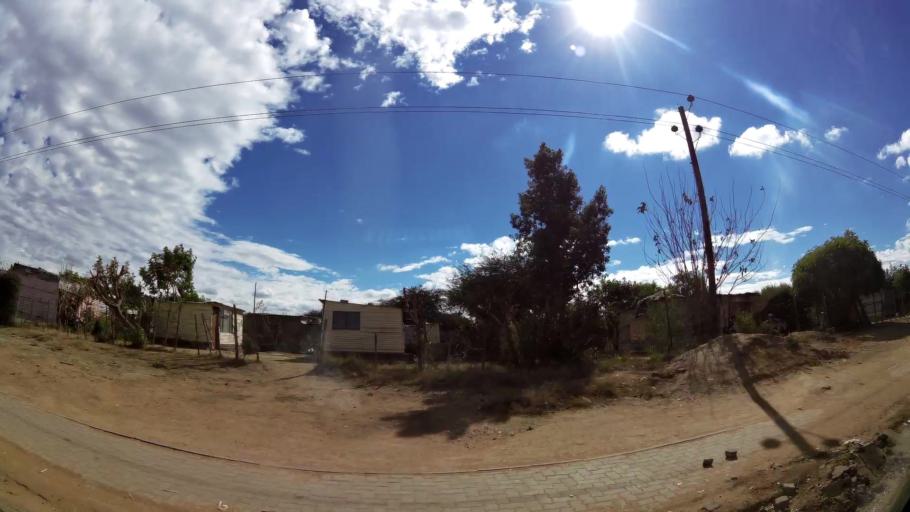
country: ZA
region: Limpopo
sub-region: Waterberg District Municipality
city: Bela-Bela
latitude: -24.8821
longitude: 28.3150
